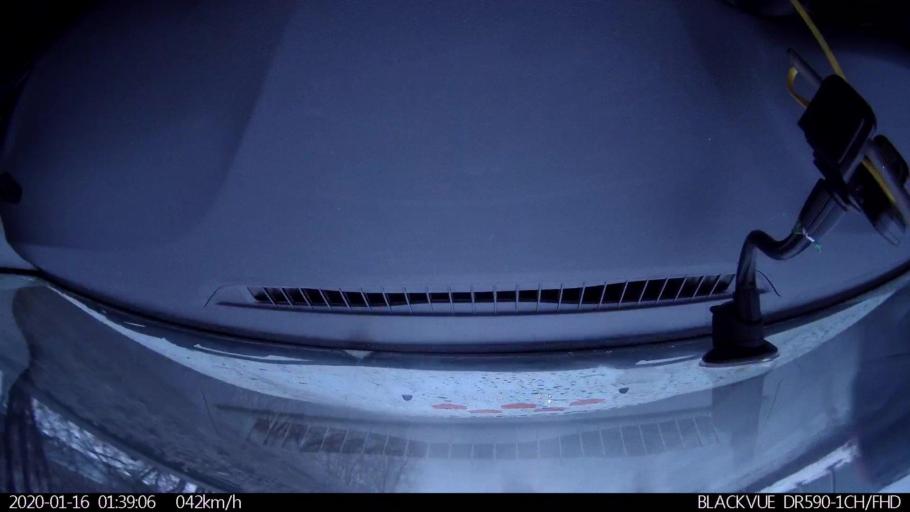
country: RU
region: Nizjnij Novgorod
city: Gorbatovka
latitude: 56.3365
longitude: 43.7974
